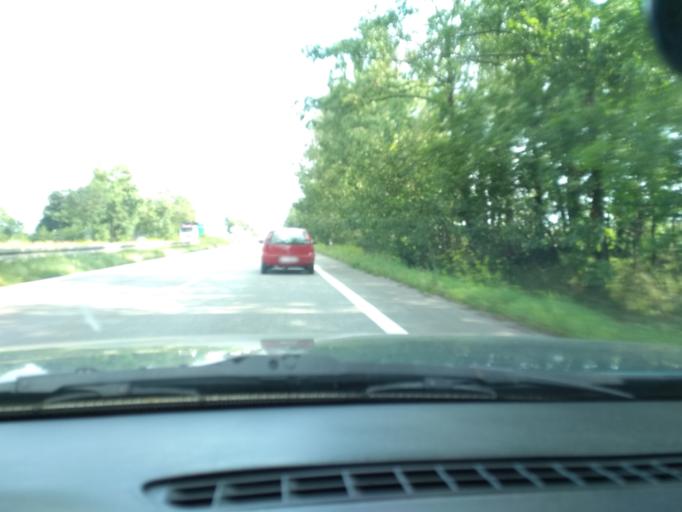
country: PL
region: Silesian Voivodeship
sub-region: Zory
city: Zory
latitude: 50.0063
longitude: 18.7098
